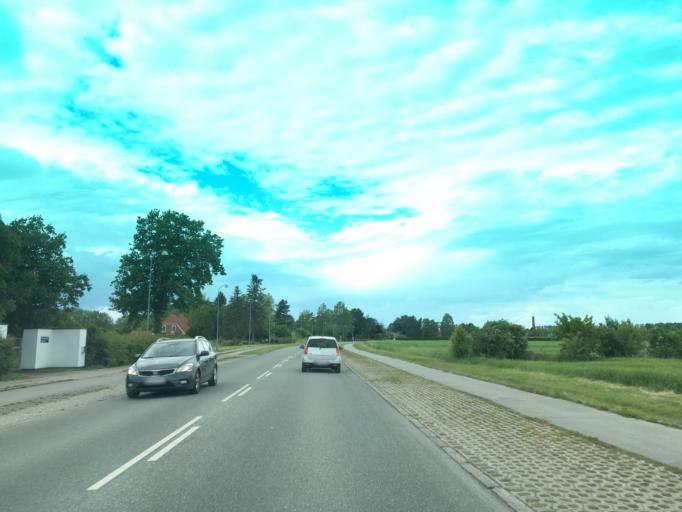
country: DK
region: Capital Region
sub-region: Hvidovre Kommune
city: Hvidovre
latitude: 55.6347
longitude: 12.4513
